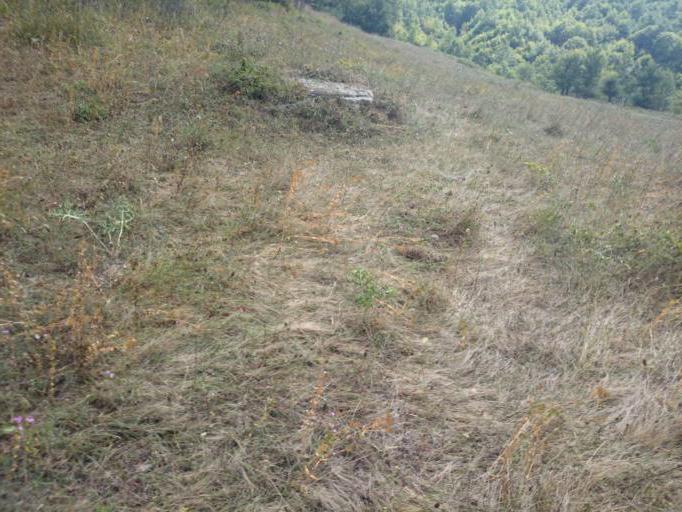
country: AL
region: Elbasan
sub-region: Rrethi i Elbasanit
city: Zavaline
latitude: 40.9534
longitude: 20.2329
